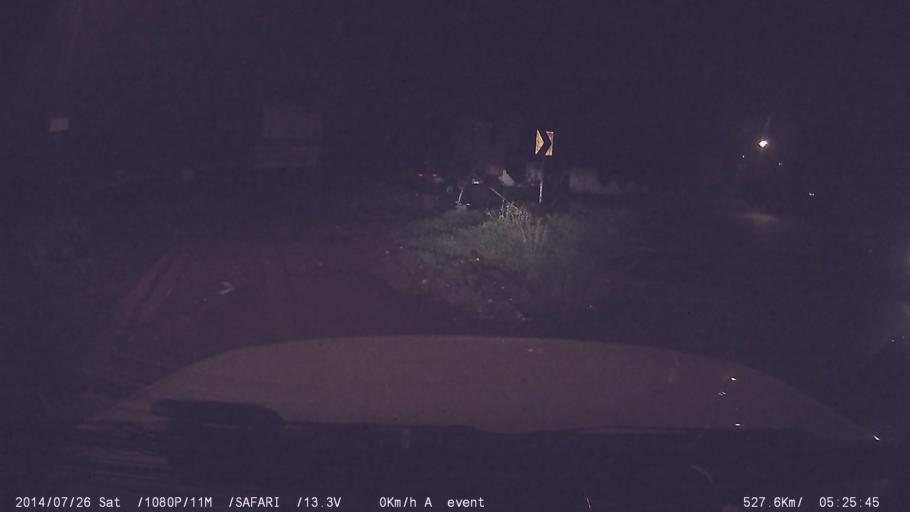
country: IN
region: Kerala
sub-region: Ernakulam
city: Muvattupuzha
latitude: 9.9733
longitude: 76.5806
